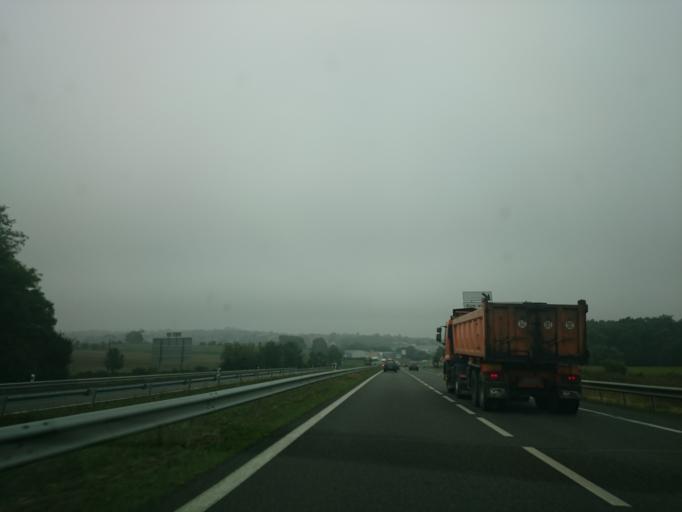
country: FR
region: Brittany
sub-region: Departement d'Ille-et-Vilaine
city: Pance
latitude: 47.8997
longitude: -1.6864
